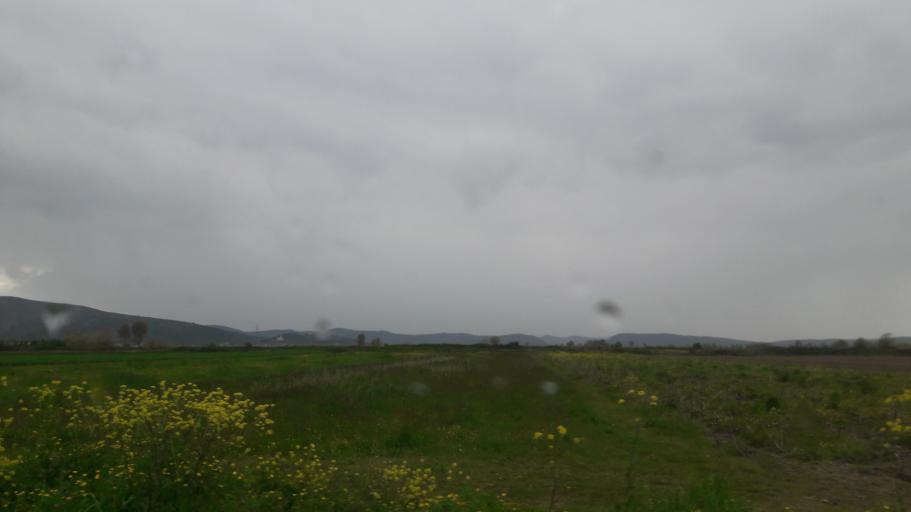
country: AL
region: Shkoder
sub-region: Rrethi i Shkodres
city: Berdica e Madhe
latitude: 41.9608
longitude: 19.5044
